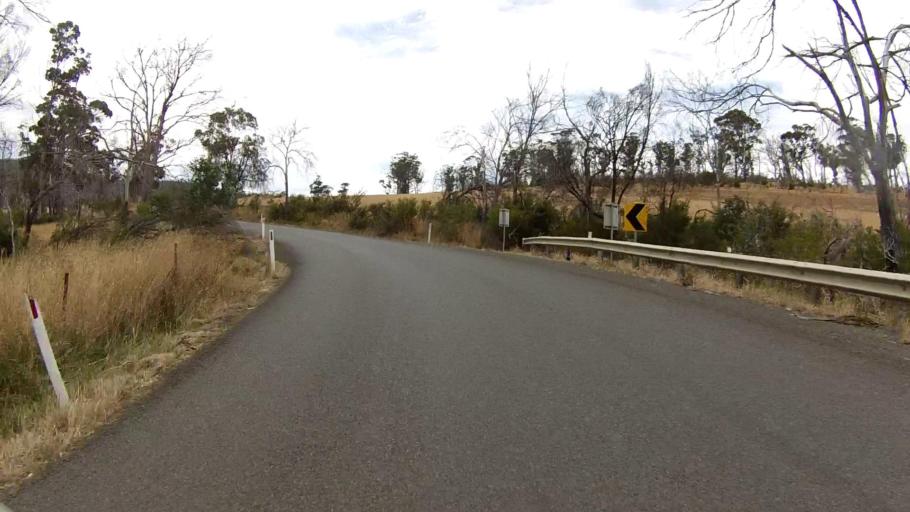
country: AU
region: Tasmania
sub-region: Sorell
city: Sorell
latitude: -42.8950
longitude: 147.7787
